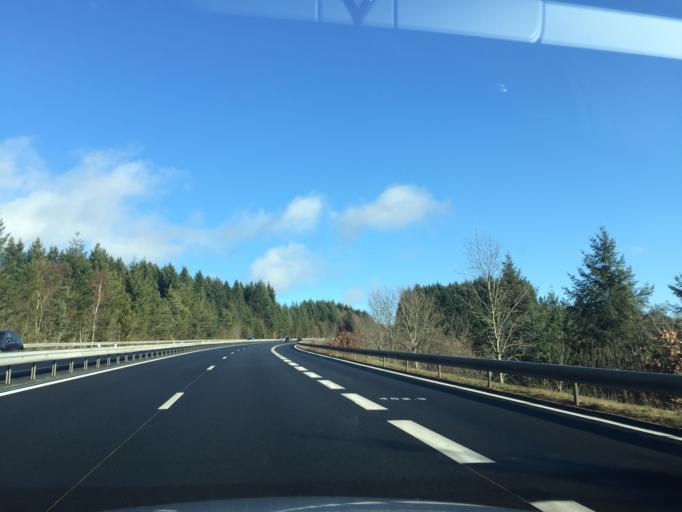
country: FR
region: Rhone-Alpes
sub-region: Departement de la Loire
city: Noiretable
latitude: 45.8460
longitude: 3.7511
